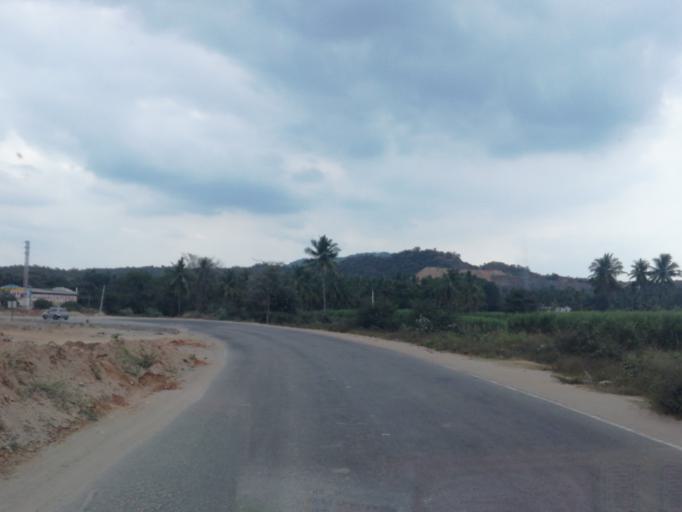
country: IN
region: Andhra Pradesh
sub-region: Chittoor
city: Ramapuram
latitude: 13.0976
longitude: 79.1255
